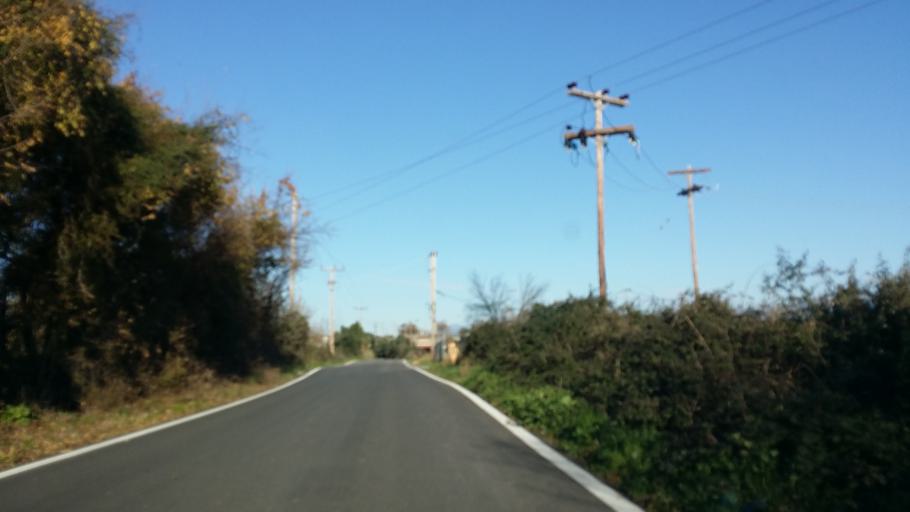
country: GR
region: West Greece
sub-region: Nomos Aitolias kai Akarnanias
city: Angelokastro
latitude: 38.6252
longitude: 21.2328
